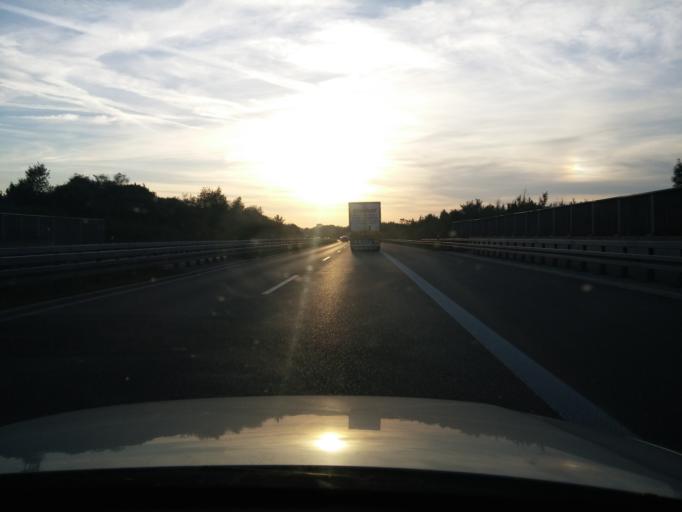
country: DE
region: Bavaria
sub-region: Swabia
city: Turkheim
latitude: 48.0386
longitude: 10.6413
